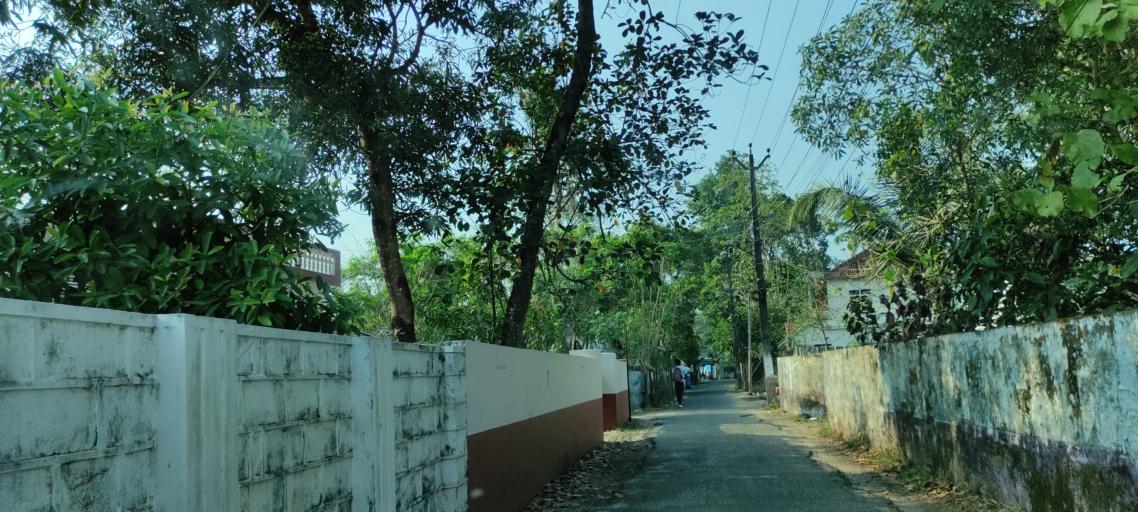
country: IN
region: Kerala
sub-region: Alappuzha
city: Alleppey
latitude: 9.5113
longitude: 76.3220
